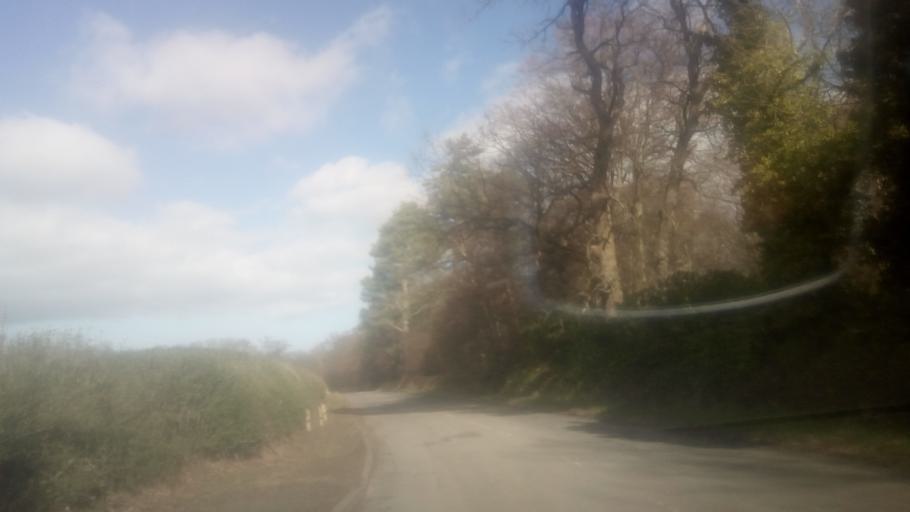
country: GB
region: Scotland
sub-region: Fife
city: Pathhead
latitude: 55.8827
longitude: -2.9595
